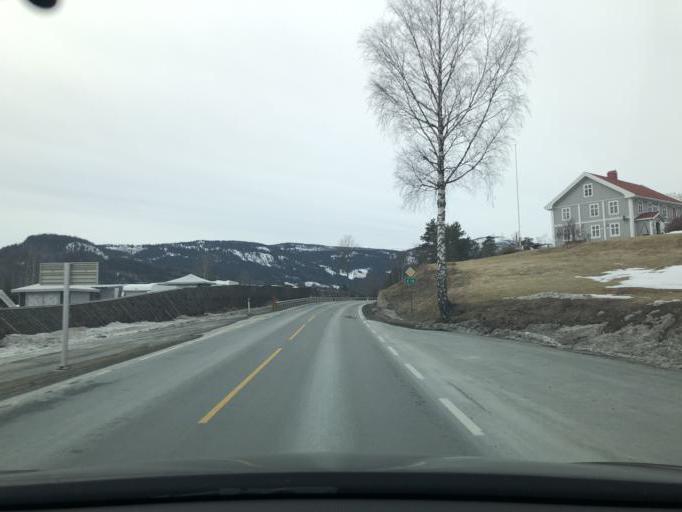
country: NO
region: Buskerud
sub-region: Ringerike
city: Honefoss
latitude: 60.4411
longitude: 10.0897
